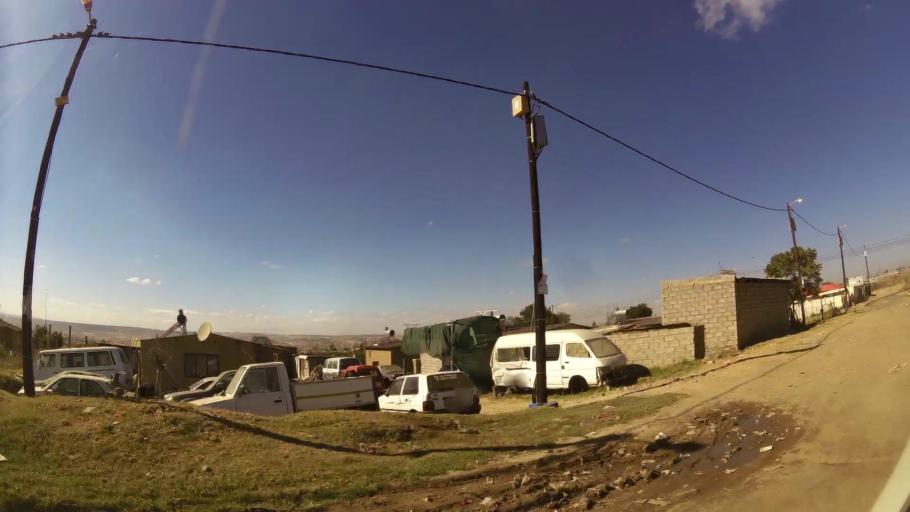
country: ZA
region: Gauteng
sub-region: City of Johannesburg Metropolitan Municipality
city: Diepsloot
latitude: -25.9195
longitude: 28.0842
